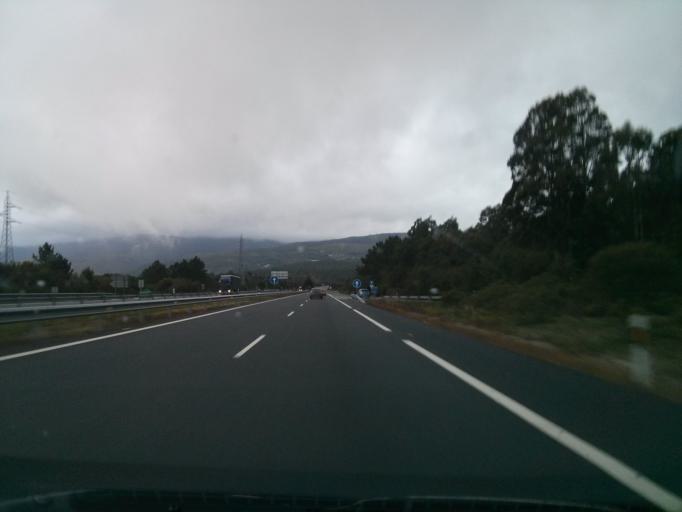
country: ES
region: Galicia
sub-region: Provincia de Ourense
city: Melon
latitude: 42.2043
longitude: -8.2721
